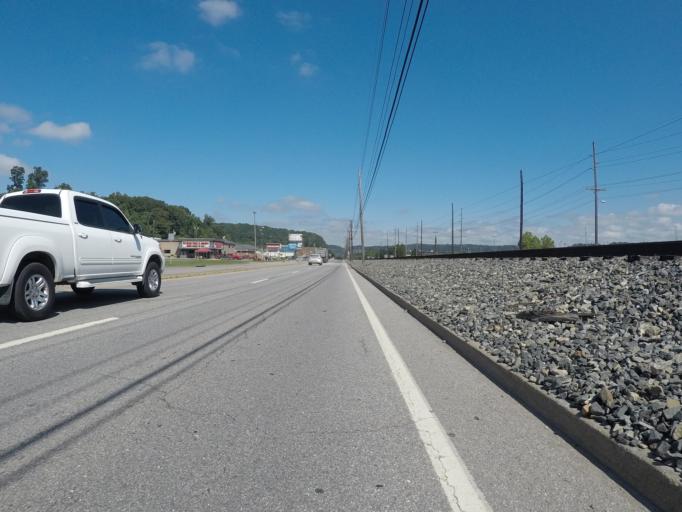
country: US
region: Kentucky
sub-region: Boyd County
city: Ashland
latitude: 38.4489
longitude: -82.6121
